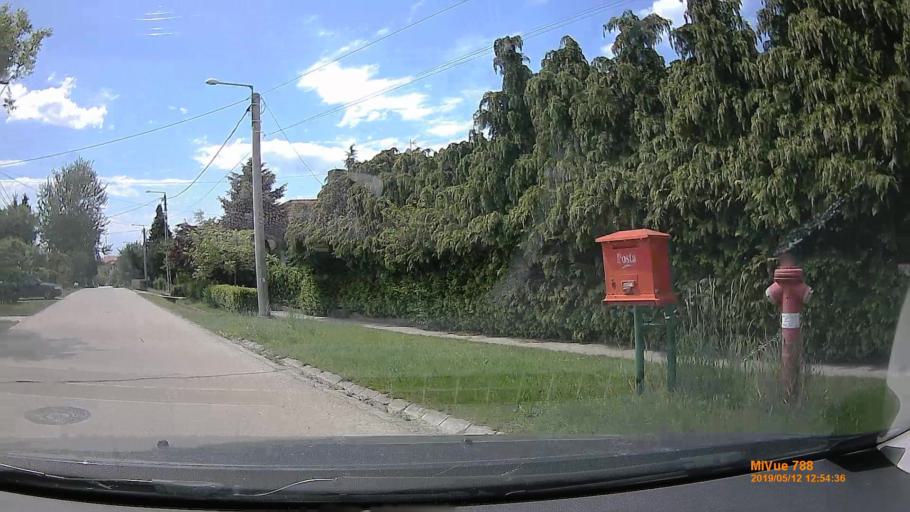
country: HU
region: Pest
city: Ecser
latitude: 47.4705
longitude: 19.3045
